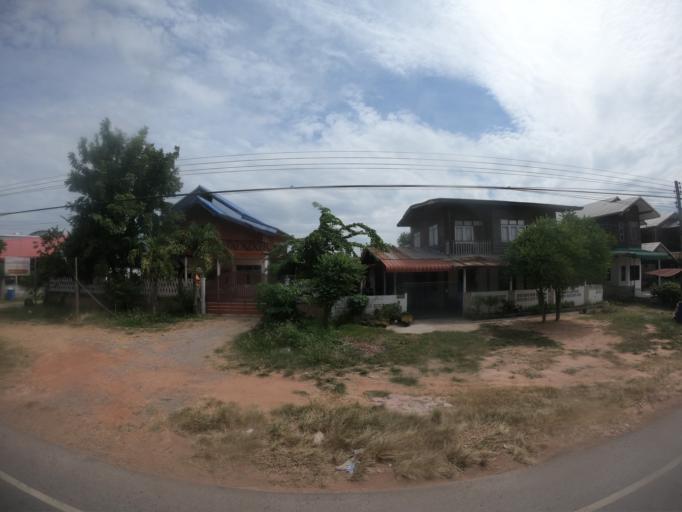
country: TH
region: Maha Sarakham
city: Chiang Yuen
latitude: 16.3983
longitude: 103.1001
